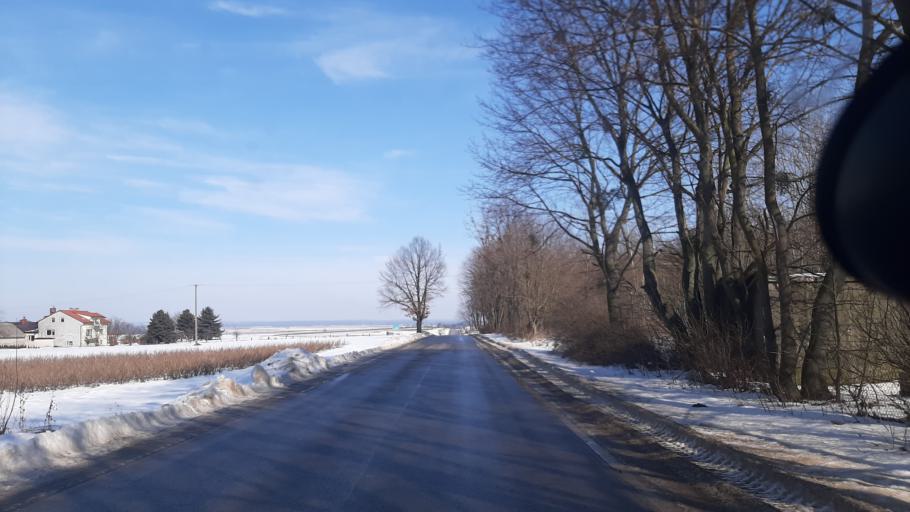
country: PL
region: Lublin Voivodeship
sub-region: Powiat pulawski
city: Kurow
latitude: 51.3628
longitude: 22.1397
